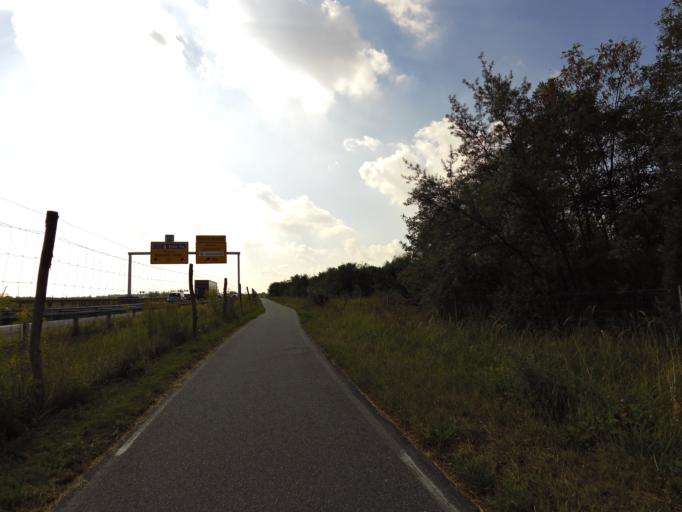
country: DE
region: Berlin
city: Lichtenrade
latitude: 52.3708
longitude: 13.4216
